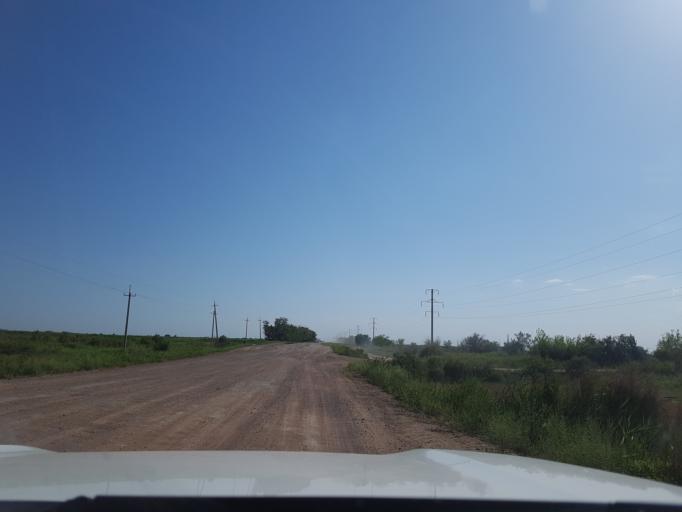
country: TM
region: Dasoguz
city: Koeneuergench
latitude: 42.1261
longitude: 58.9396
